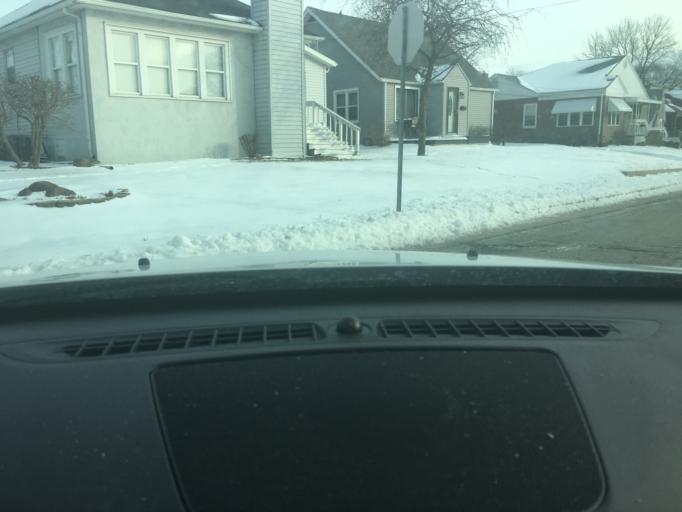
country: US
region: Illinois
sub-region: LaSalle County
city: Peru
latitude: 41.3378
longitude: -89.1144
